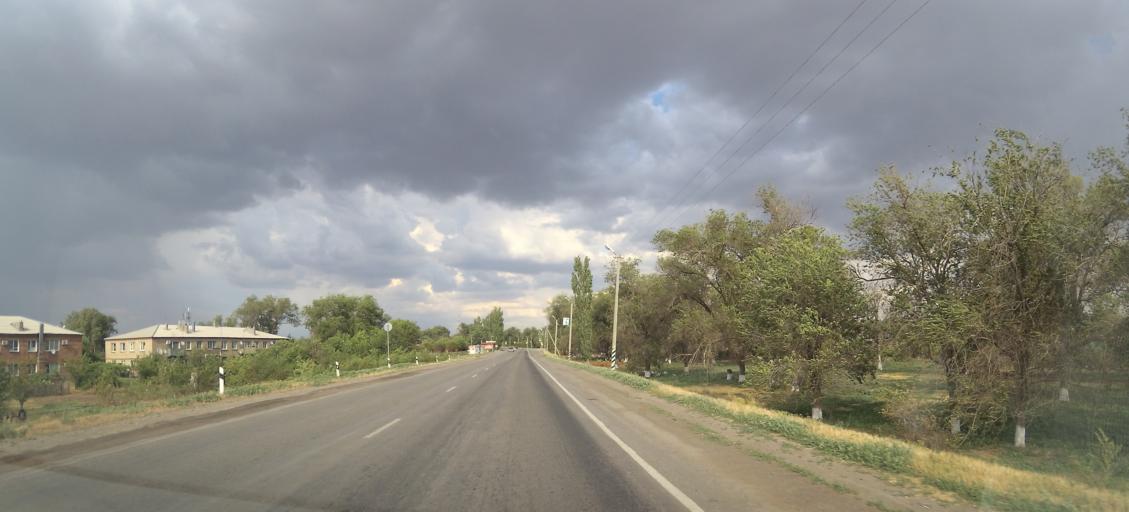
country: RU
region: Rostov
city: Zimovniki
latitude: 47.1460
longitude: 42.4523
